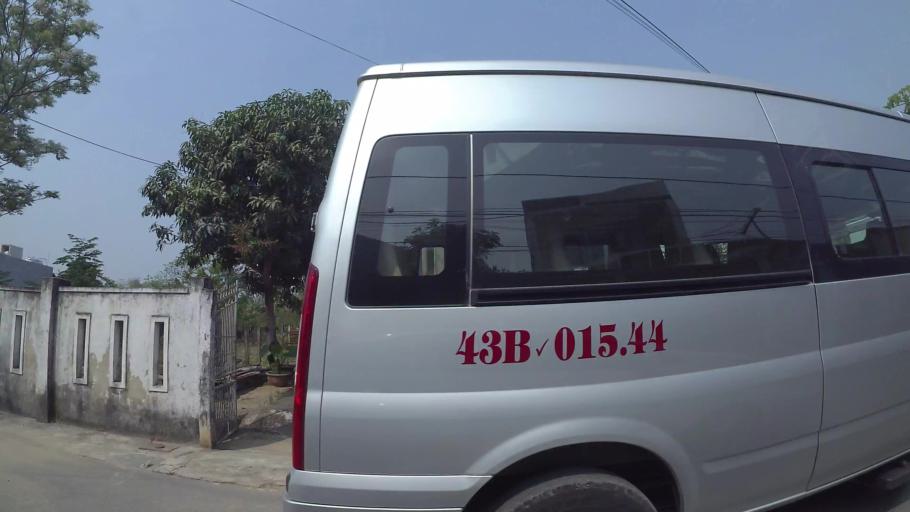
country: VN
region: Da Nang
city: Ngu Hanh Son
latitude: 15.9955
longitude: 108.2385
